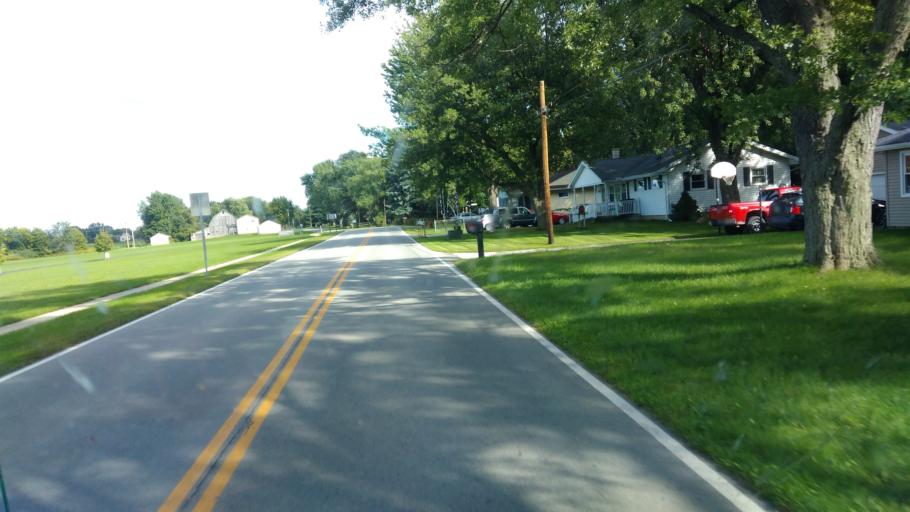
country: US
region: Ohio
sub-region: Sandusky County
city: Clyde
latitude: 41.2865
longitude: -82.9713
